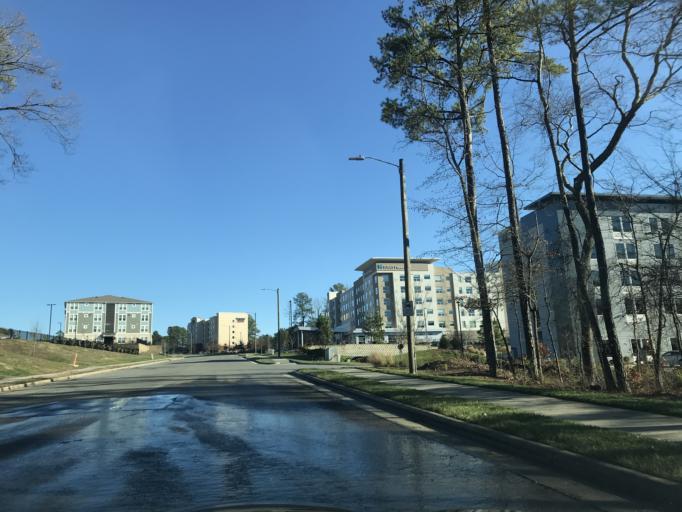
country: US
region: North Carolina
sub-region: Wake County
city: Morrisville
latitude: 35.8964
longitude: -78.8080
